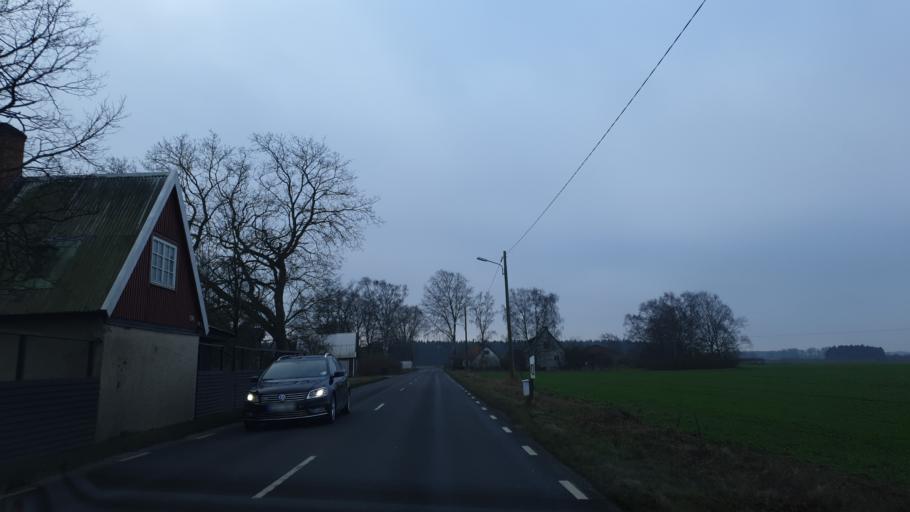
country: SE
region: Skane
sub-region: Kristianstads Kommun
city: Fjalkinge
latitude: 56.0135
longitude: 14.3706
